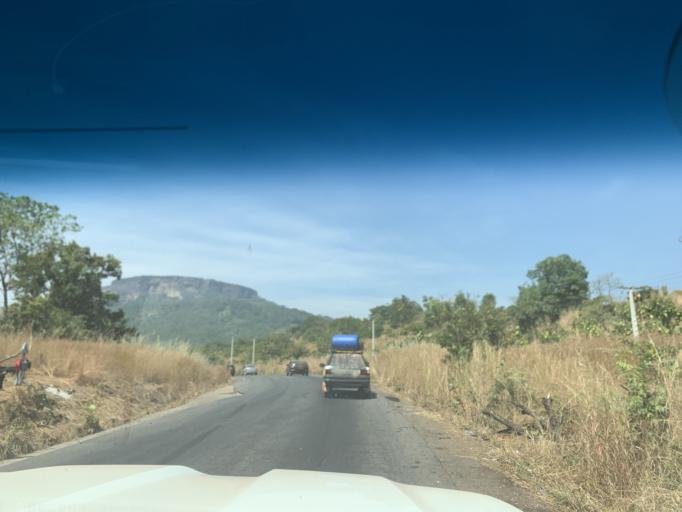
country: GN
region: Kindia
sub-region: Kindia
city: Kindia
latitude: 10.1324
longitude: -12.5415
